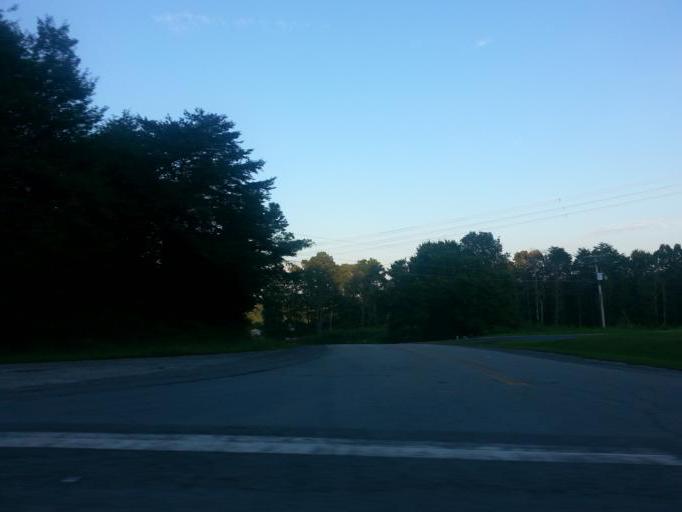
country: US
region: Tennessee
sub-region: Roane County
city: Midtown
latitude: 35.8297
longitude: -84.5455
